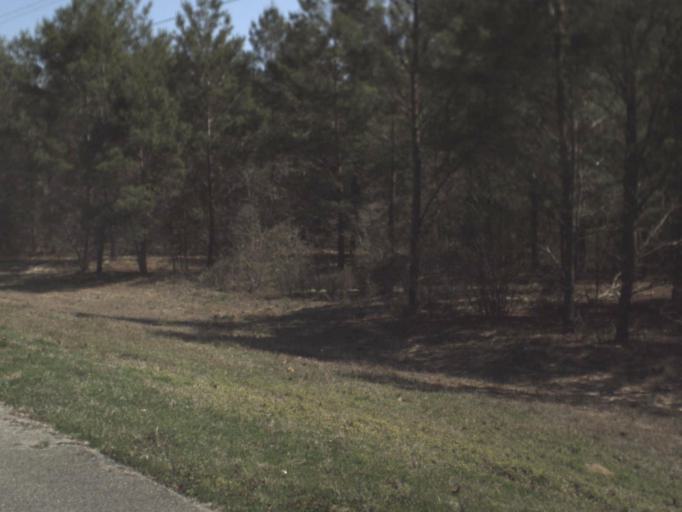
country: US
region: Florida
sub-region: Liberty County
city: Bristol
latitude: 30.4905
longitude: -84.9026
